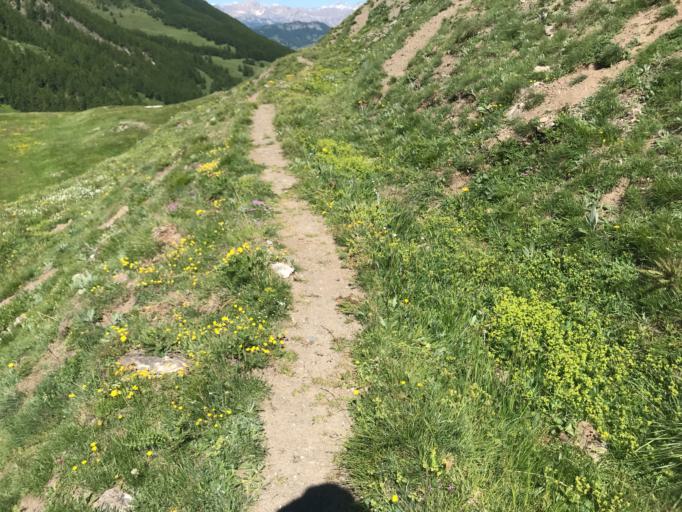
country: IT
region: Piedmont
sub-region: Provincia di Cuneo
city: Pontechianale
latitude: 44.7094
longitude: 6.9286
